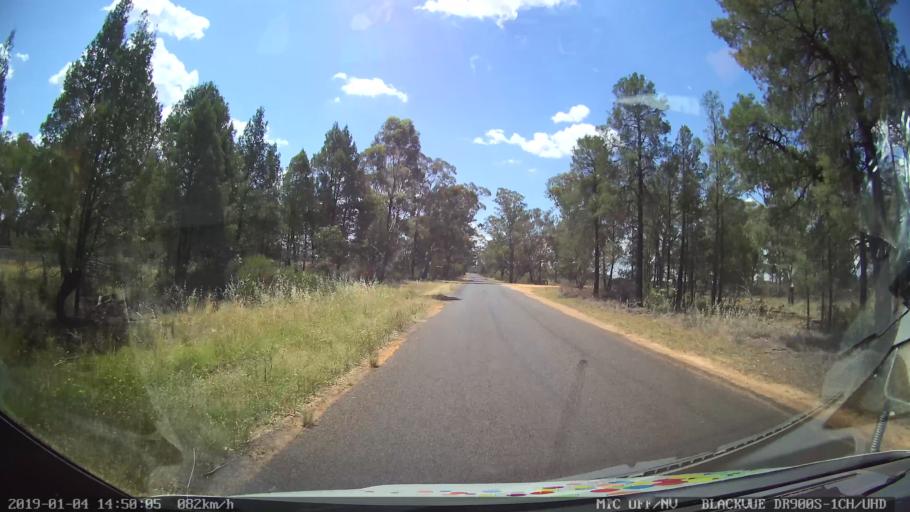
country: AU
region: New South Wales
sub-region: Dubbo Municipality
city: Dubbo
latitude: -32.0418
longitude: 148.6594
